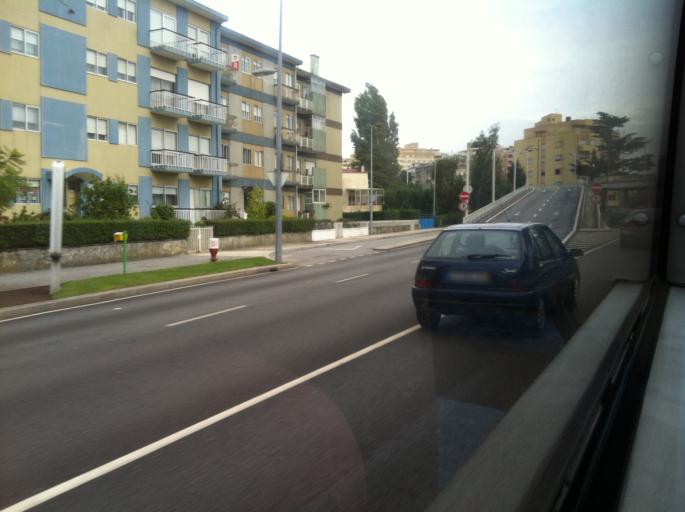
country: PT
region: Porto
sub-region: Matosinhos
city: Senhora da Hora
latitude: 41.1641
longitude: -8.6354
